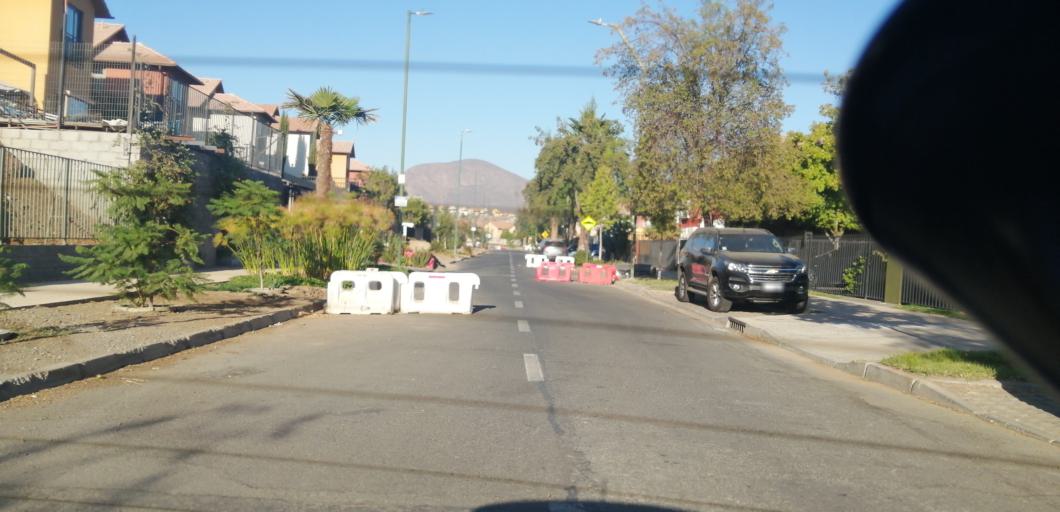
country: CL
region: Santiago Metropolitan
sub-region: Provincia de Santiago
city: Lo Prado
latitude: -33.4514
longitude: -70.8432
